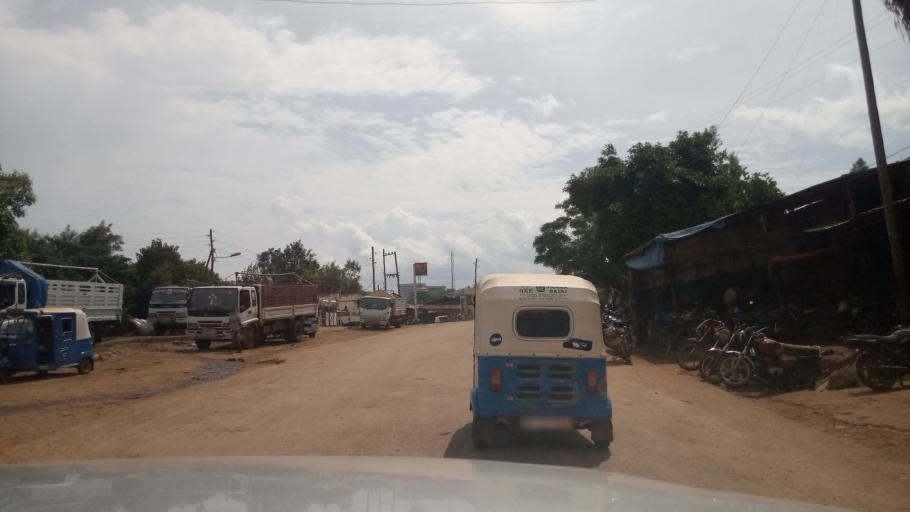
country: ET
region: Oromiya
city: Agaro
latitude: 7.8545
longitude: 36.5913
